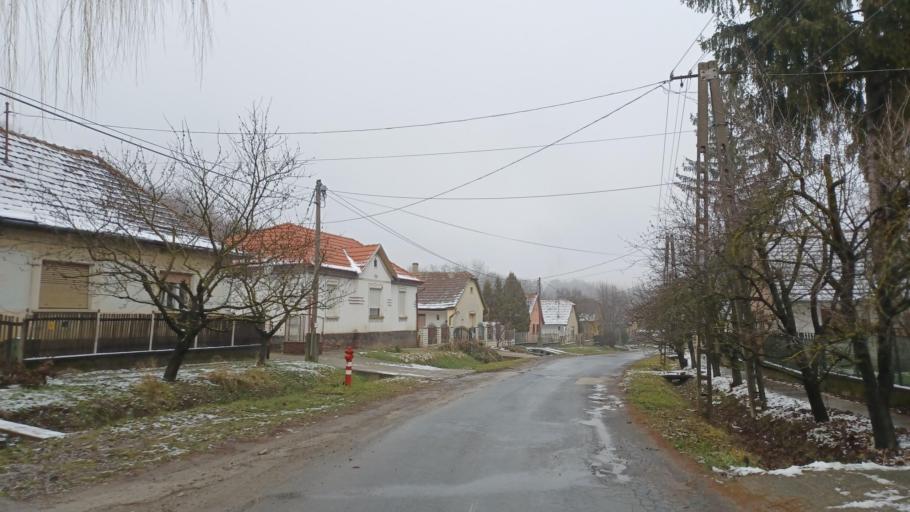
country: HU
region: Tolna
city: Pincehely
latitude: 46.6298
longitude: 18.4778
